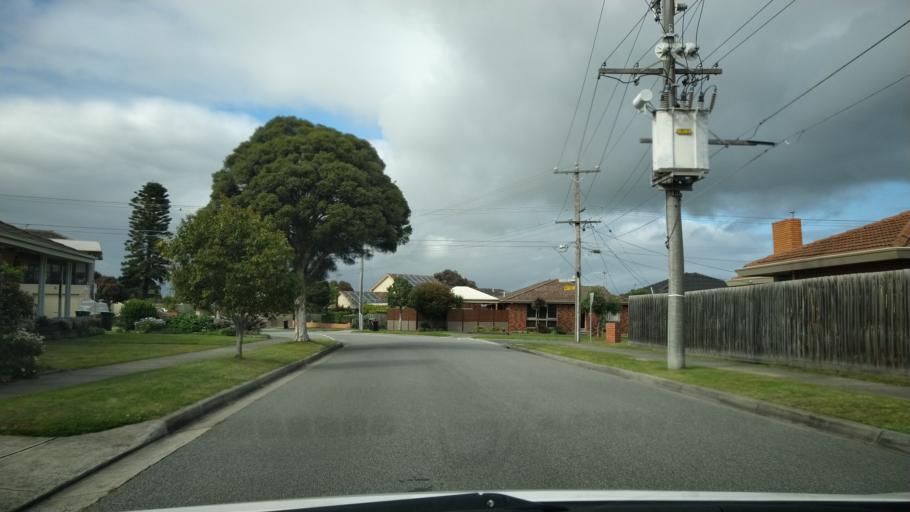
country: AU
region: Victoria
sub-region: Greater Dandenong
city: Keysborough
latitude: -37.9911
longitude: 145.1773
